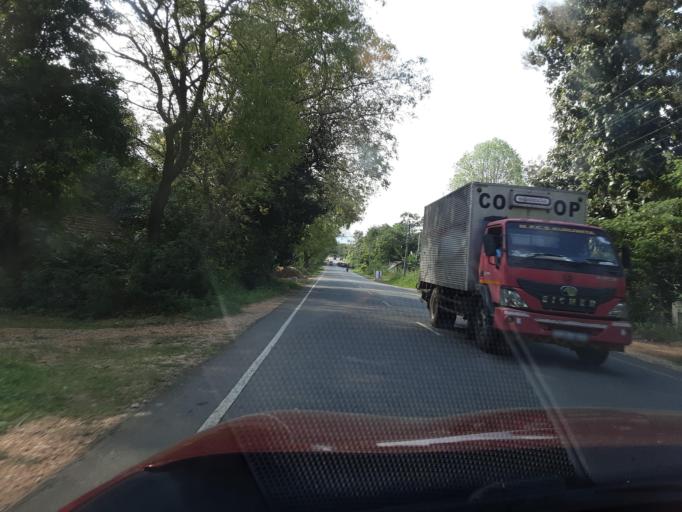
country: LK
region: Uva
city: Haputale
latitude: 6.6058
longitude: 81.1362
